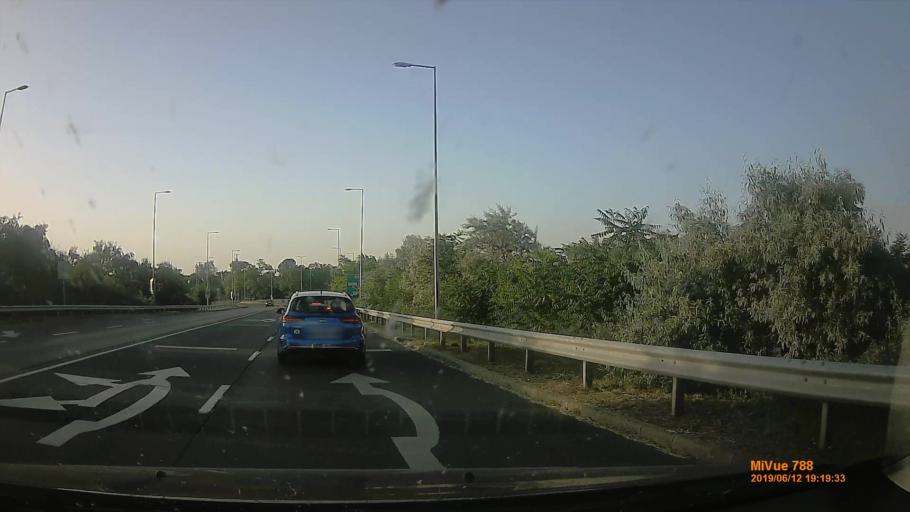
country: HU
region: Bacs-Kiskun
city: Kecskemet
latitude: 46.8992
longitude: 19.7037
